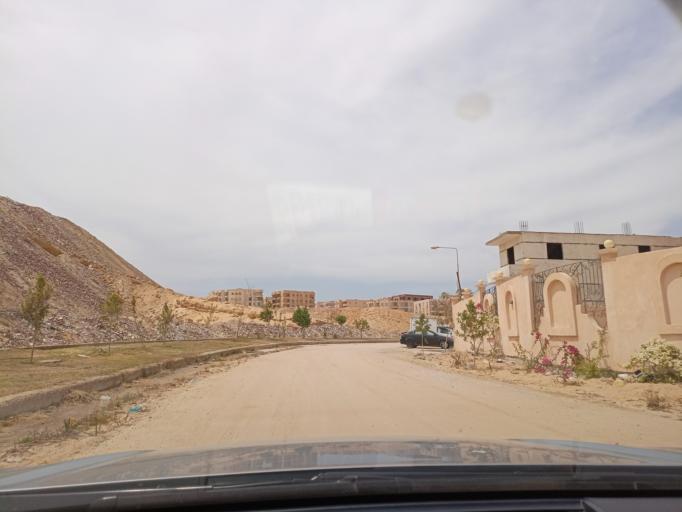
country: EG
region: Muhafazat al Qalyubiyah
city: Al Khankah
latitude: 30.2354
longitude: 31.4859
